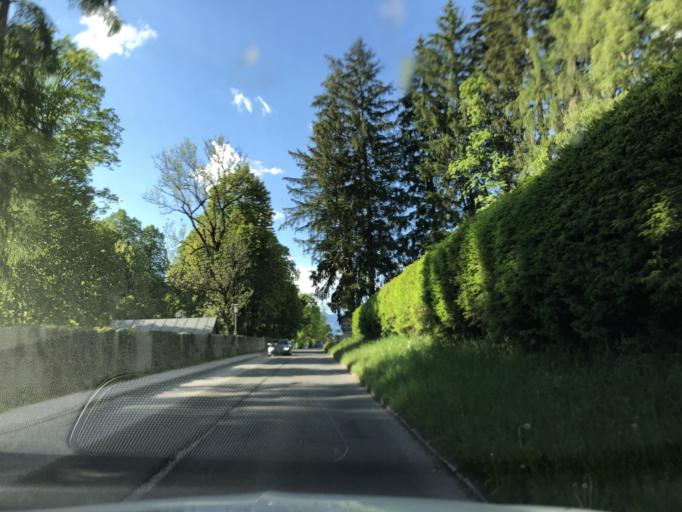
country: AT
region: Salzburg
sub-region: Politischer Bezirk Zell am See
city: Zell am See
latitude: 47.3128
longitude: 12.8159
